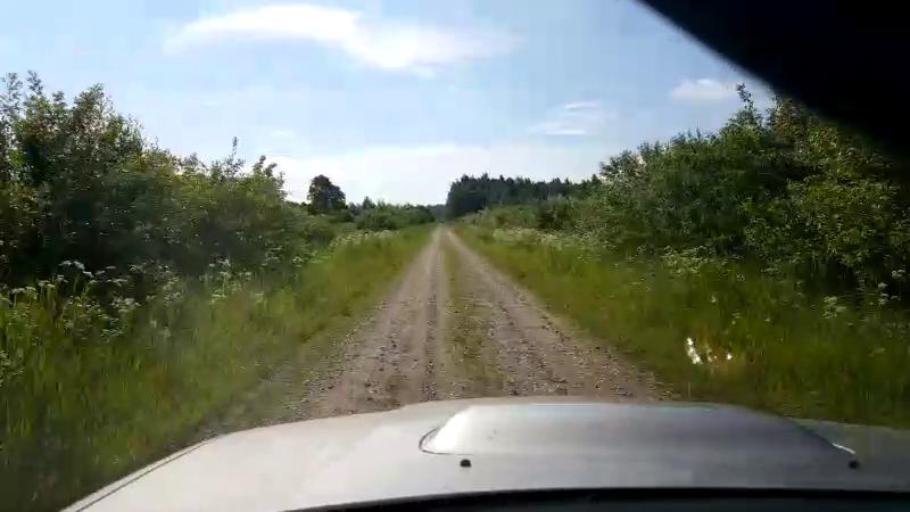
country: EE
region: Paernumaa
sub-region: Sindi linn
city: Sindi
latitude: 58.4938
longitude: 24.6649
